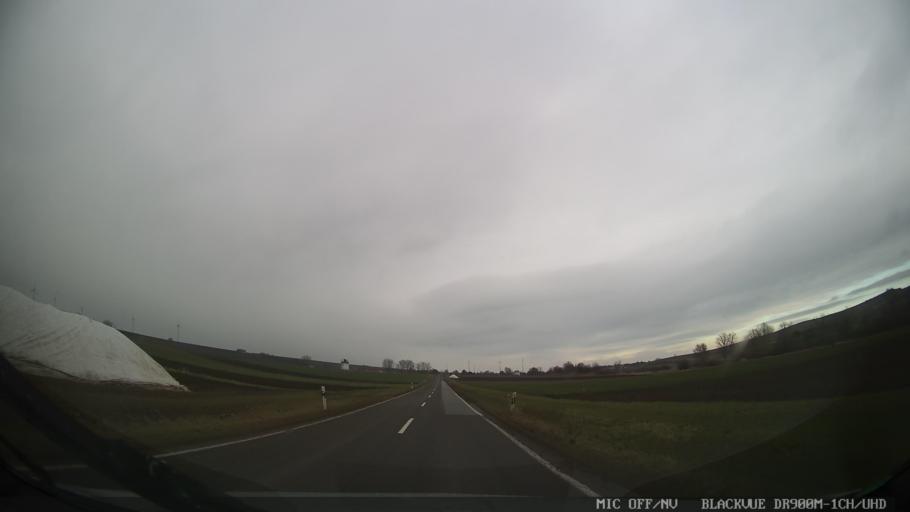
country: DE
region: Rheinland-Pfalz
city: Biebelnheim
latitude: 49.7927
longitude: 8.1803
